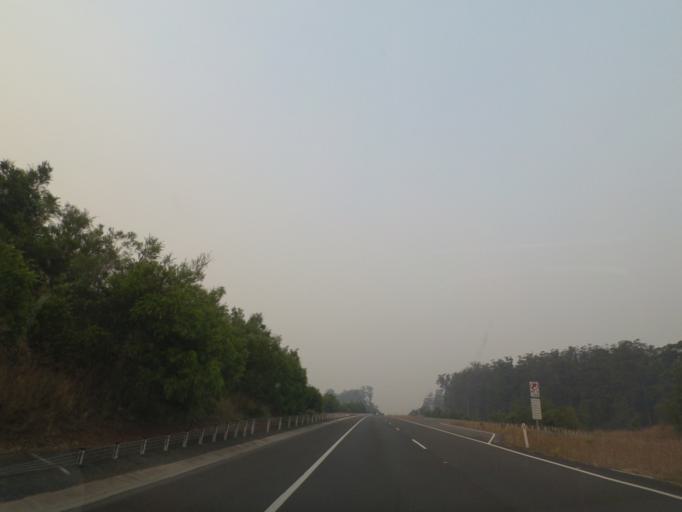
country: AU
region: New South Wales
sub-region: Nambucca Shire
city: Macksville
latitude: -30.7766
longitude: 152.8952
